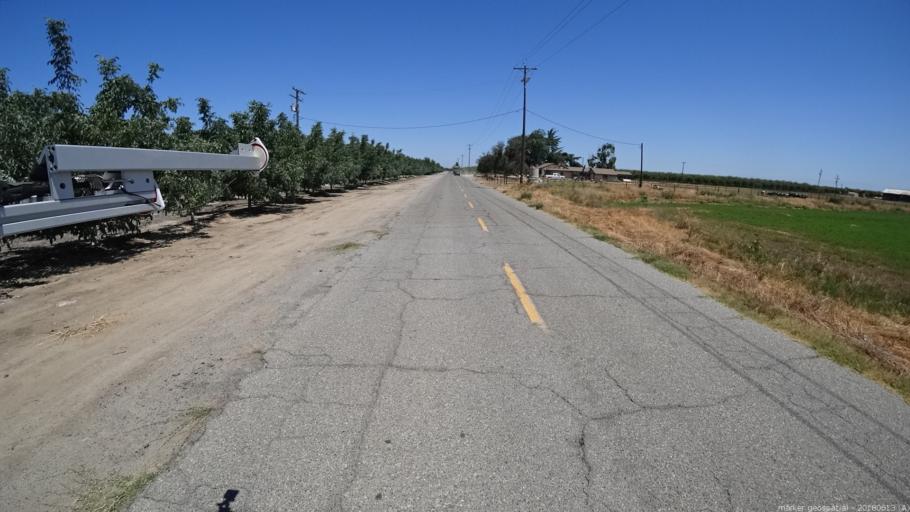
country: US
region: California
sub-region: Madera County
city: Chowchilla
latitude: 37.0424
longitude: -120.3106
